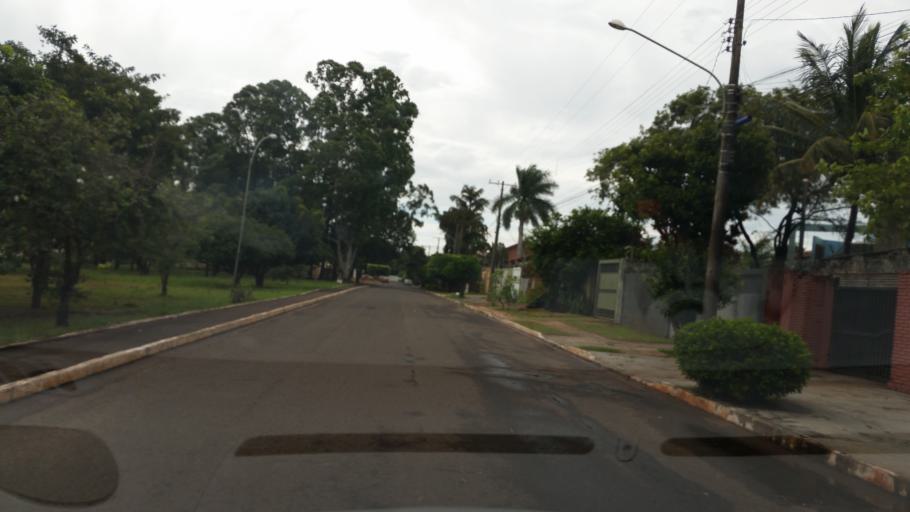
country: BR
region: Mato Grosso do Sul
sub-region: Campo Grande
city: Campo Grande
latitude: -20.4605
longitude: -54.5671
